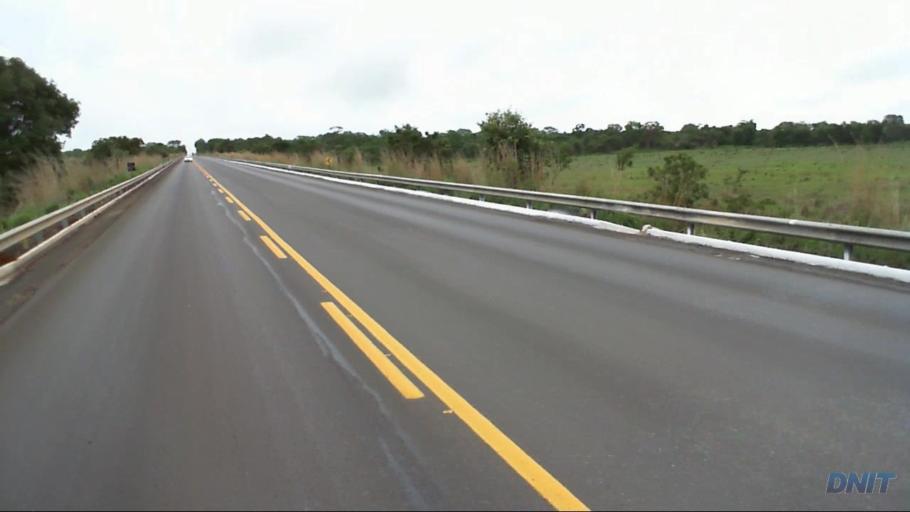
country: BR
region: Goias
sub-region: Padre Bernardo
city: Padre Bernardo
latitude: -15.1766
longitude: -48.4089
